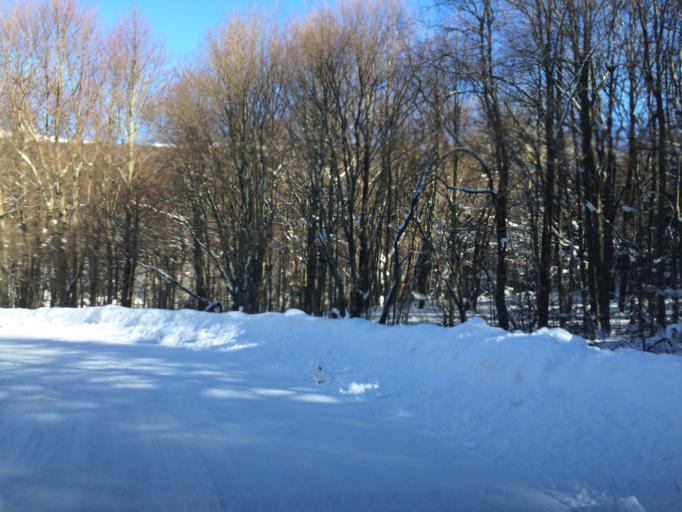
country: PL
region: Subcarpathian Voivodeship
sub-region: Powiat bieszczadzki
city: Lutowiska
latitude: 49.1417
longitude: 22.5383
